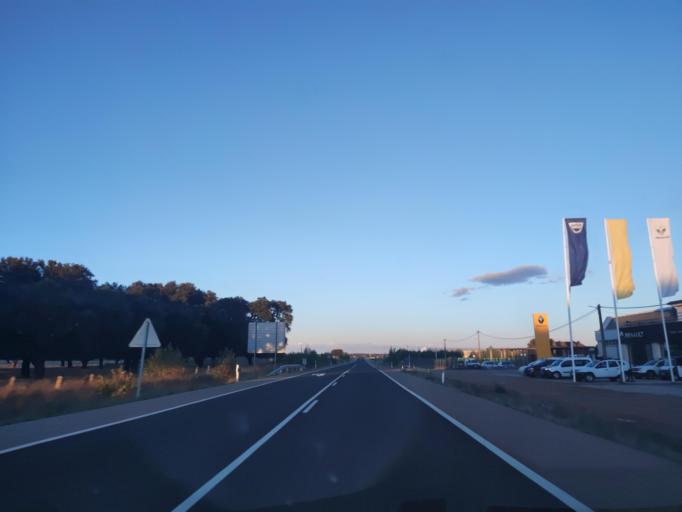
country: ES
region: Castille and Leon
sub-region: Provincia de Salamanca
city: La Fuente de San Esteban
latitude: 40.7931
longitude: -6.2415
